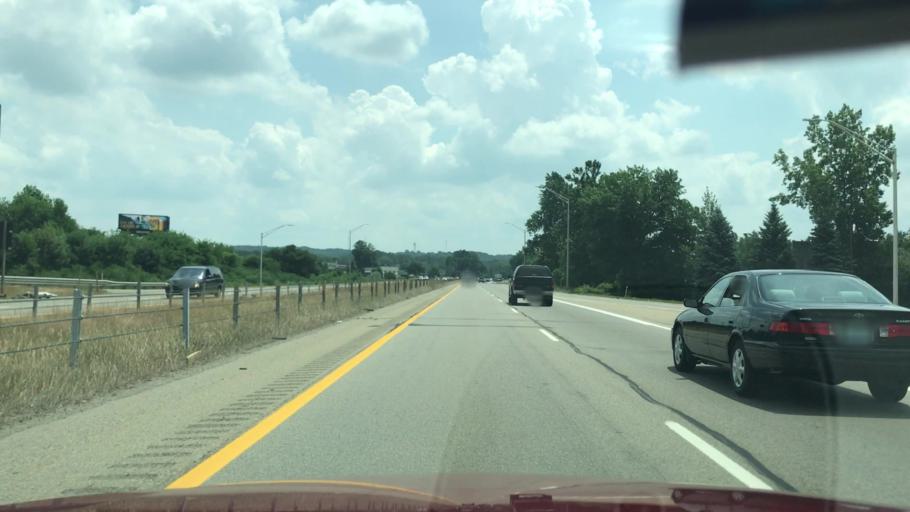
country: US
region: Michigan
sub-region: Kent County
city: Cutlerville
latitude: 42.8255
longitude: -85.6717
